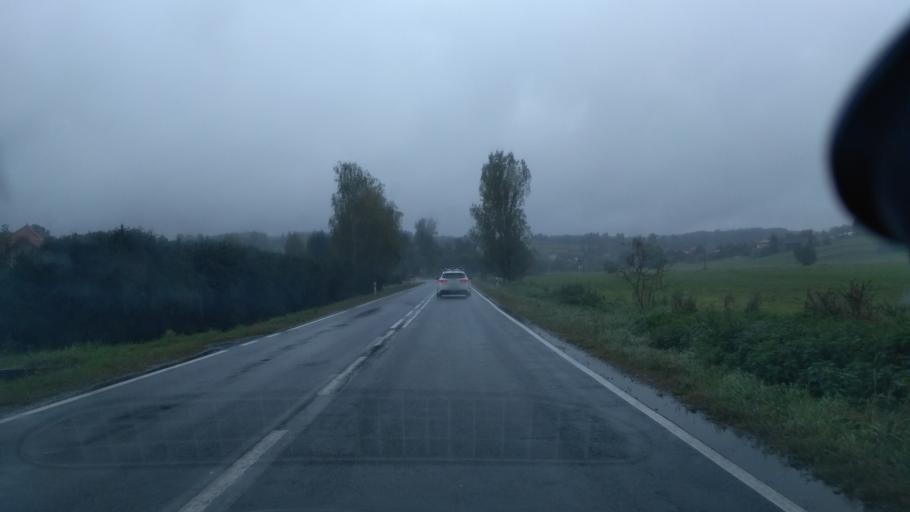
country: PL
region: Subcarpathian Voivodeship
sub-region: Powiat ropczycko-sedziszowski
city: Niedzwiada
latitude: 49.9752
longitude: 21.5681
